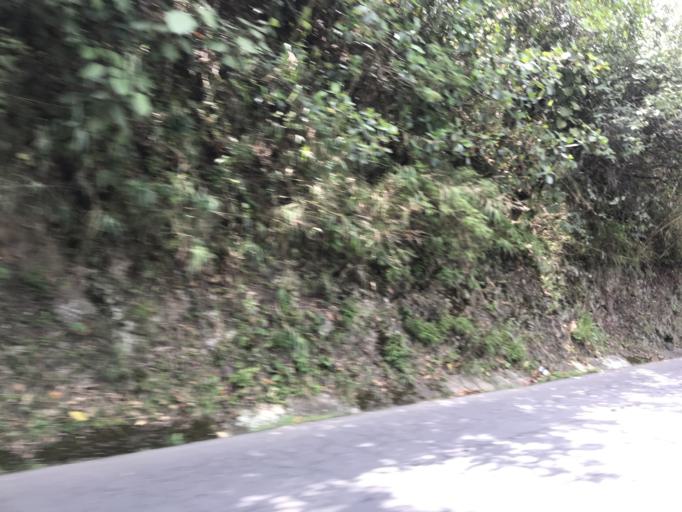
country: CO
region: Huila
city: San Agustin
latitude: 1.8754
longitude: -76.2502
